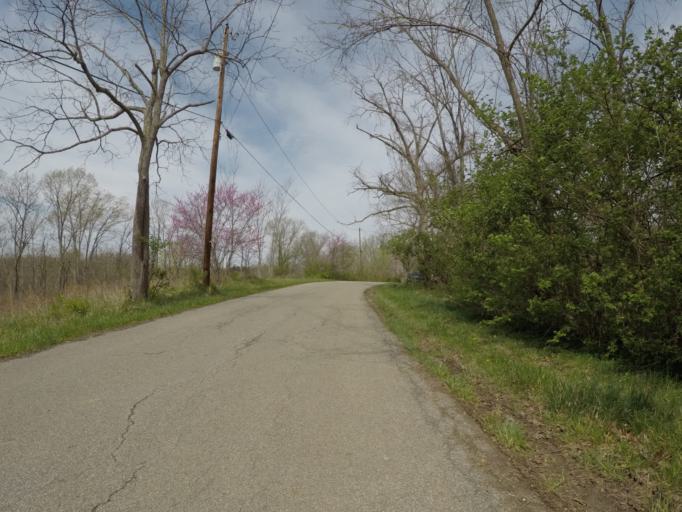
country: US
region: West Virginia
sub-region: Wayne County
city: Lavalette
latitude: 38.3461
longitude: -82.3892
